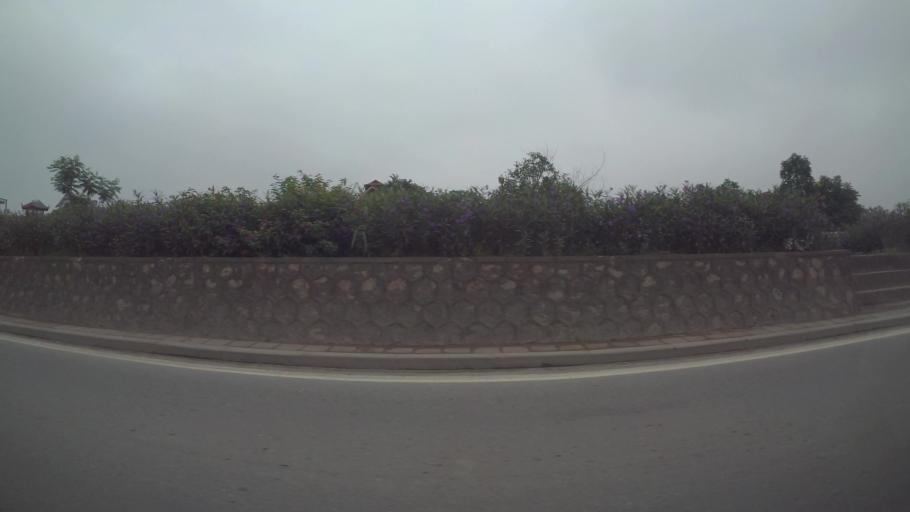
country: VN
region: Hung Yen
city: Van Giang
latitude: 20.9802
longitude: 105.8935
